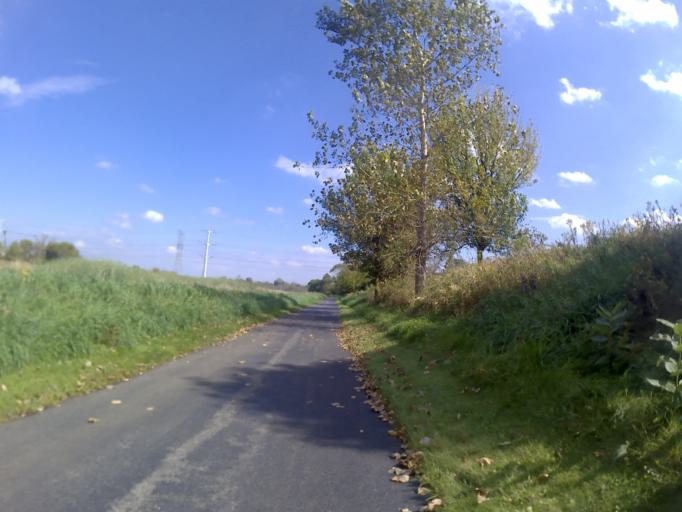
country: US
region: Illinois
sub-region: Will County
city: Bolingbrook
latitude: 41.7108
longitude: -88.1003
